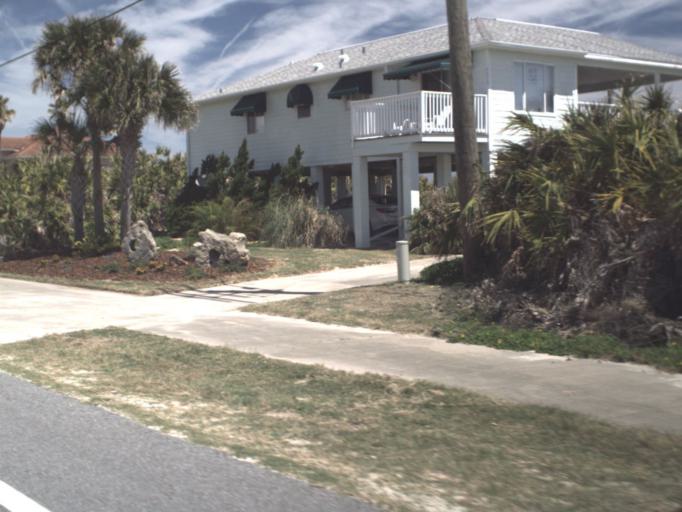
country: US
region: Florida
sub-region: Flagler County
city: Palm Coast
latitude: 29.6565
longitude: -81.2081
